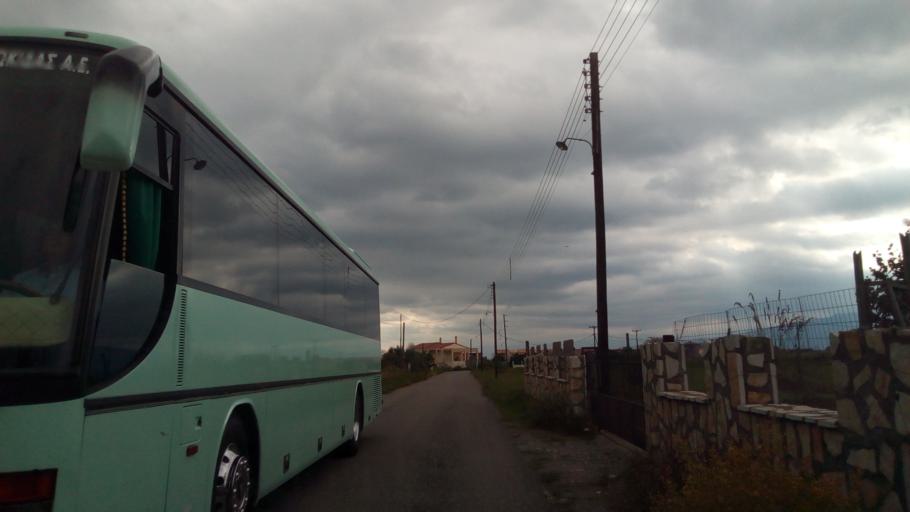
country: GR
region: West Greece
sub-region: Nomos Aitolias kai Akarnanias
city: Nafpaktos
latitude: 38.3956
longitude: 21.9149
